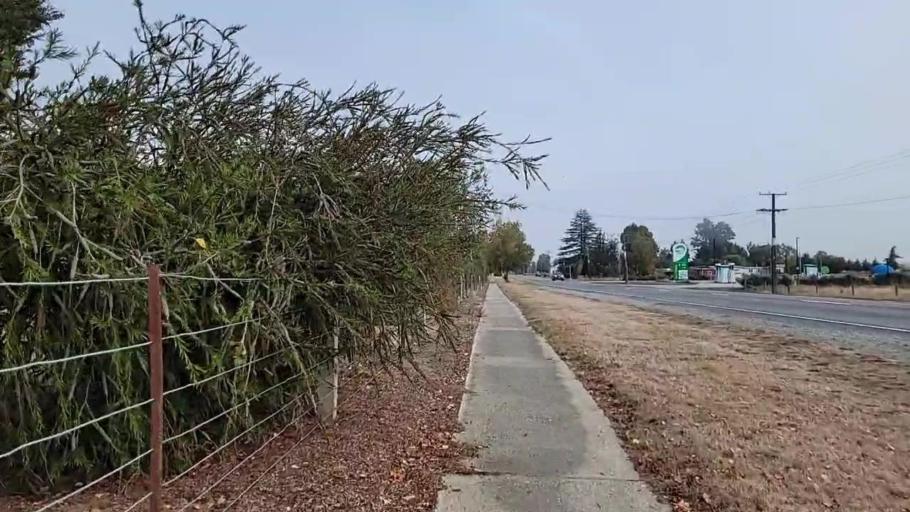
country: NZ
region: Southland
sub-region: Gore District
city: Gore
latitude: -45.6401
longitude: 169.3714
